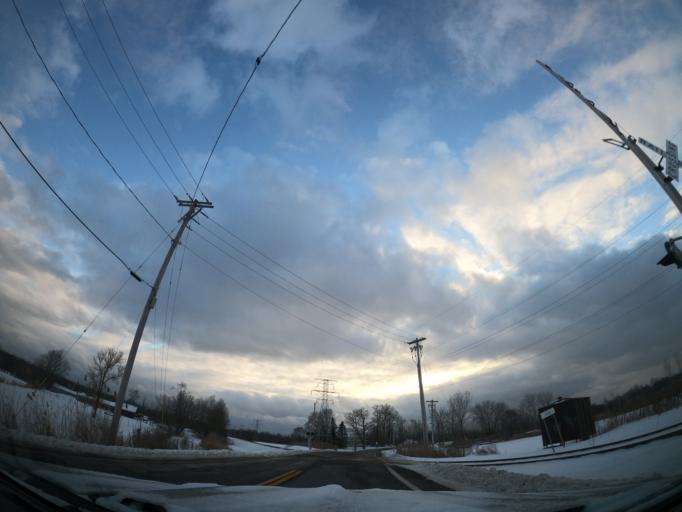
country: US
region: New York
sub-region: Onondaga County
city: Brewerton
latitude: 43.2076
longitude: -76.1621
